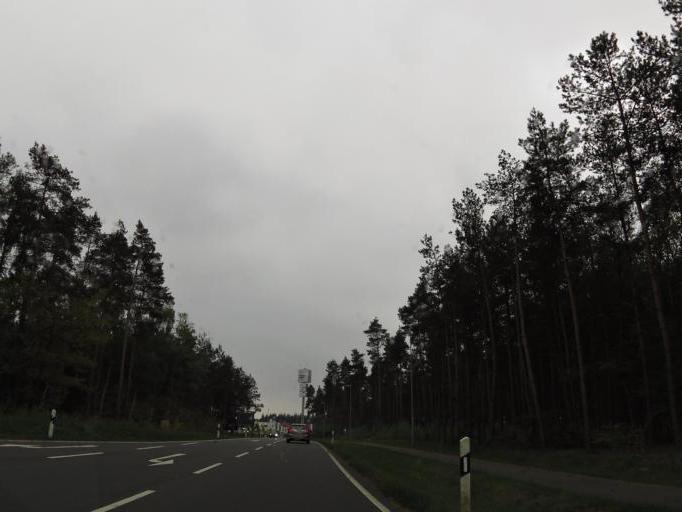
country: DE
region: Lower Saxony
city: Soltau
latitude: 52.9864
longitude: 9.9265
